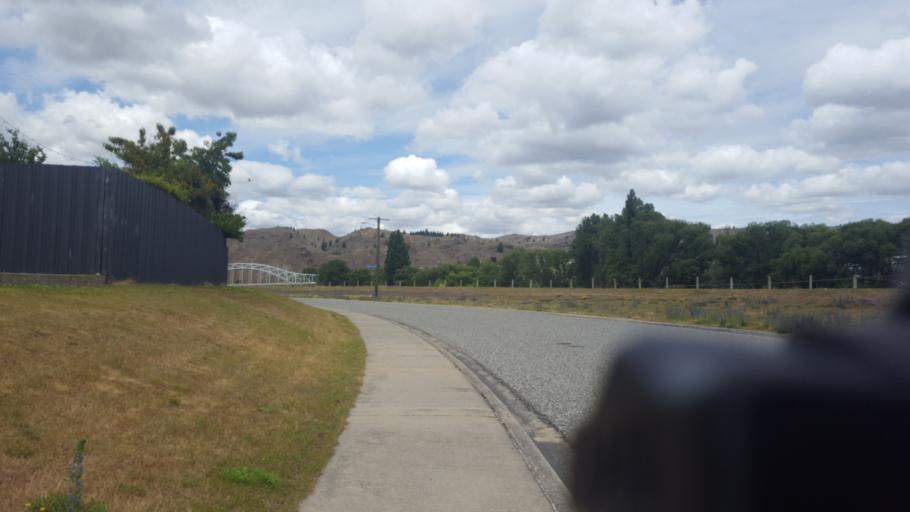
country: NZ
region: Otago
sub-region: Queenstown-Lakes District
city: Wanaka
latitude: -45.2549
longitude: 169.3853
